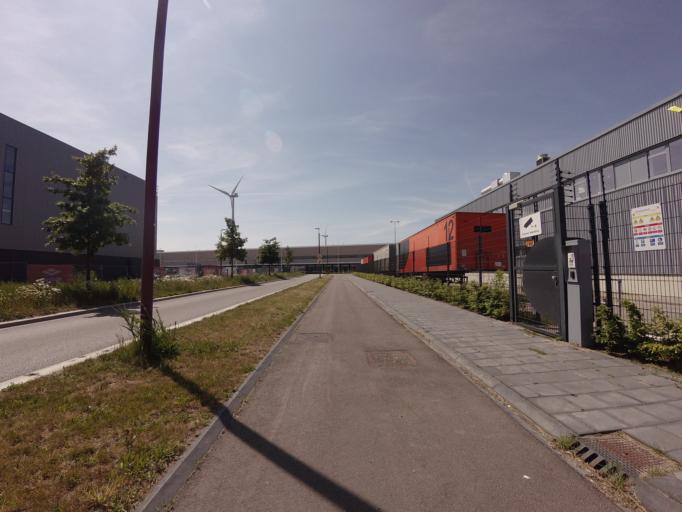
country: NL
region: Utrecht
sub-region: Gemeente Vianen
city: Vianen
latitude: 52.0214
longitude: 5.1215
